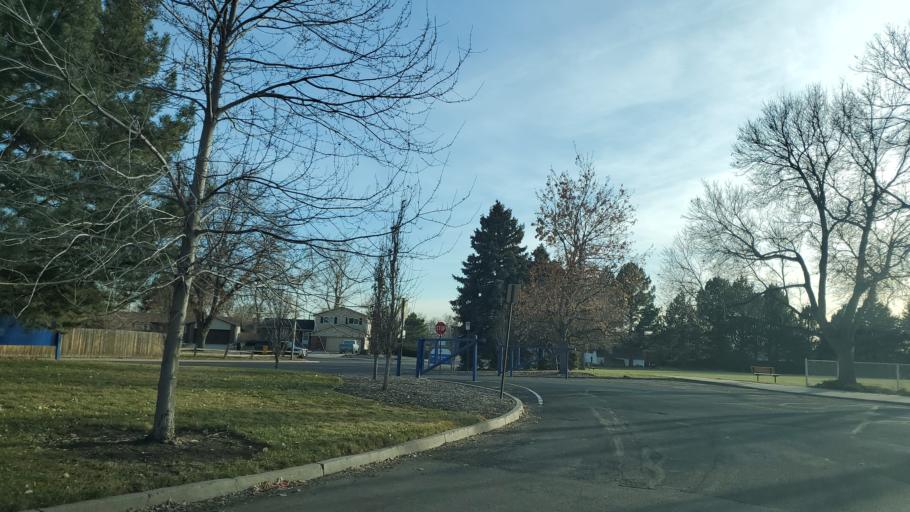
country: US
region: Colorado
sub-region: Adams County
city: Thornton
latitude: 39.9057
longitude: -104.9464
